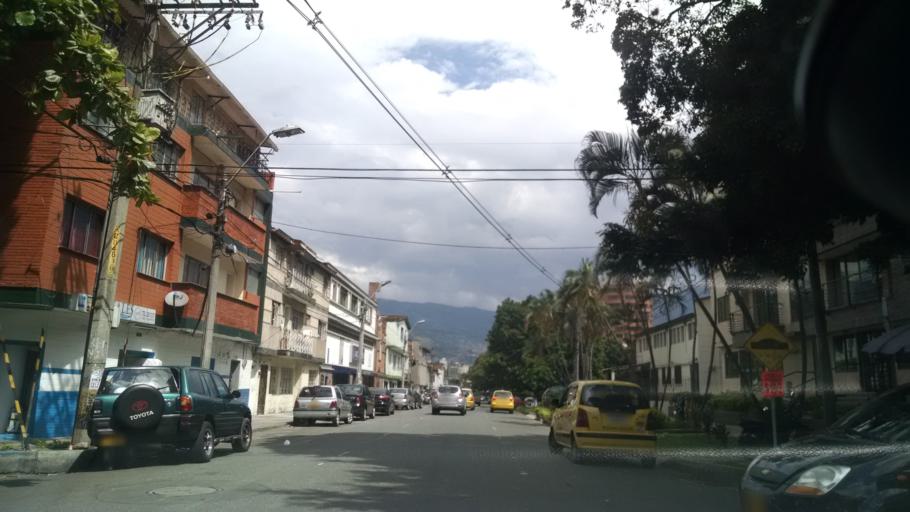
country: CO
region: Antioquia
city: Medellin
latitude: 6.2482
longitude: -75.5861
